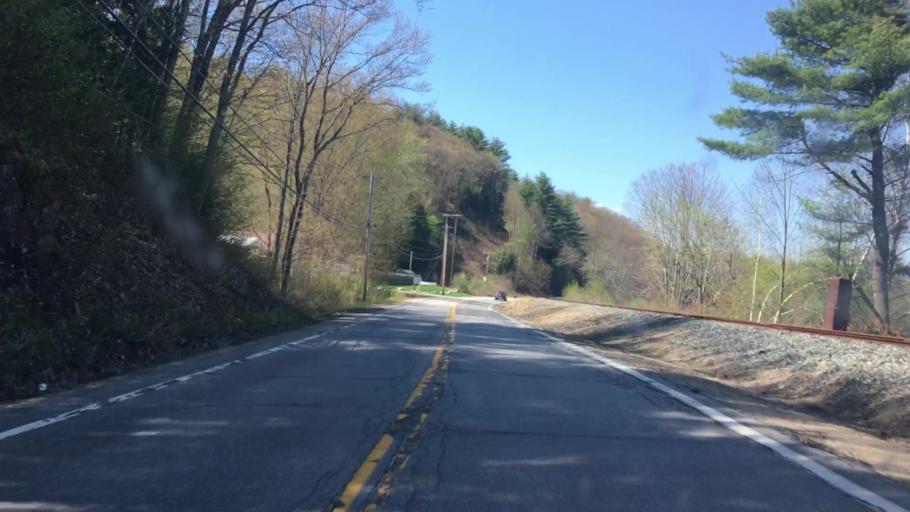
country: US
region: New Hampshire
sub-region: Grafton County
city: Plymouth
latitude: 43.7394
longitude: -71.6768
